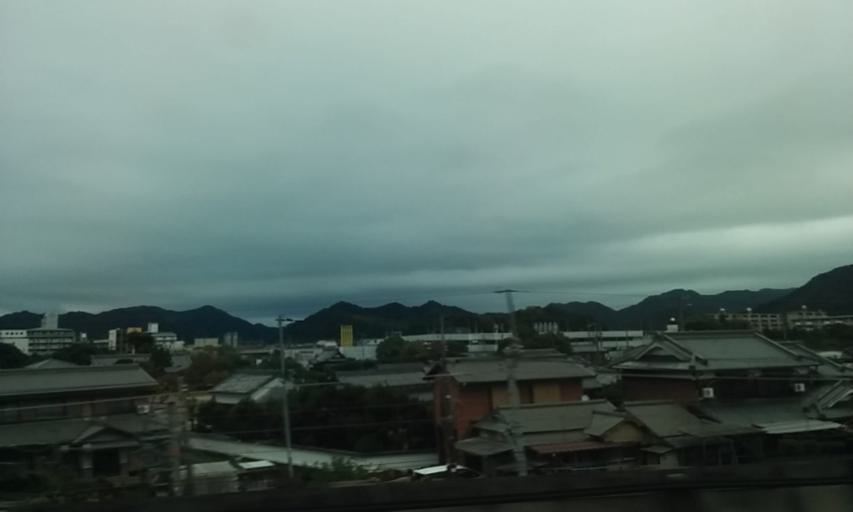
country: JP
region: Hyogo
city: Himeji
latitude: 34.8191
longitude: 134.7312
